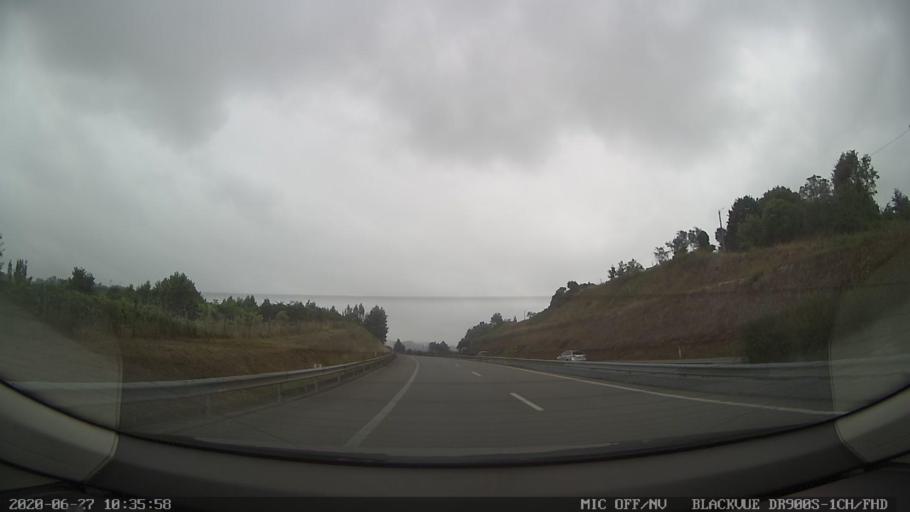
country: PT
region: Porto
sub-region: Marco de Canaveses
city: Marco de Canavezes
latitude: 41.2209
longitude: -8.1622
